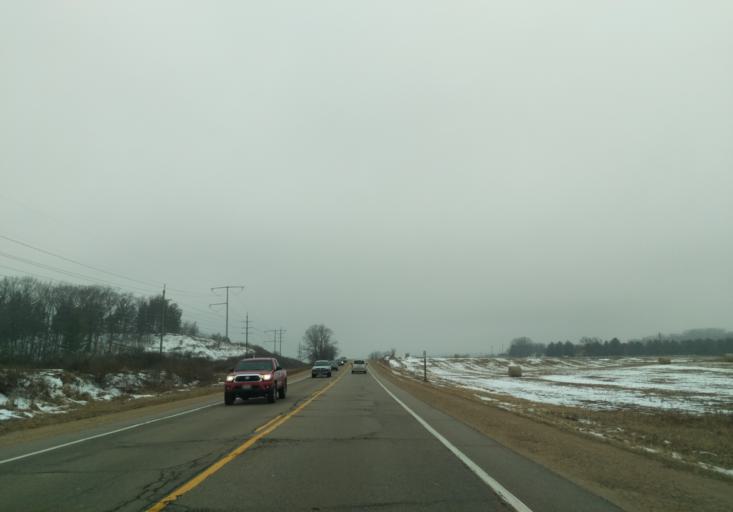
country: US
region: Wisconsin
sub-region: Dane County
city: Middleton
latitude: 43.0956
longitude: -89.5569
